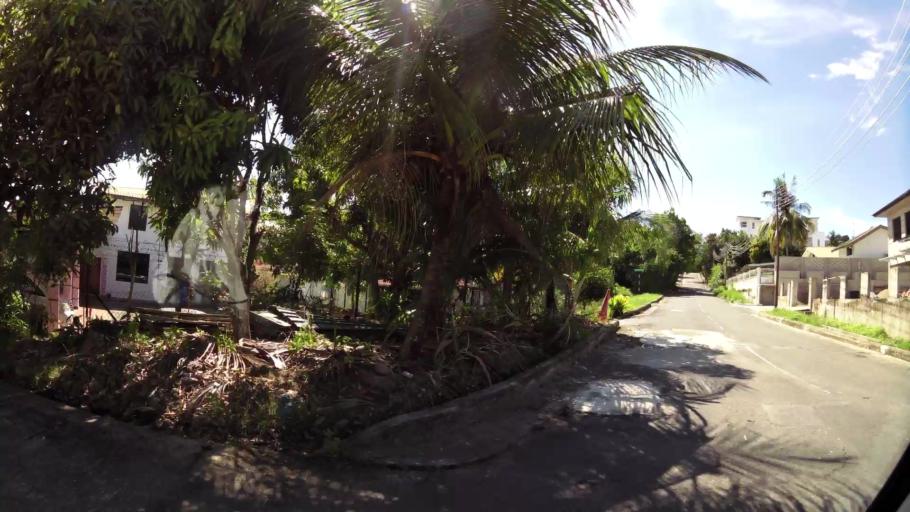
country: BN
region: Brunei and Muara
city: Bandar Seri Begawan
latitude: 4.9554
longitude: 114.9469
